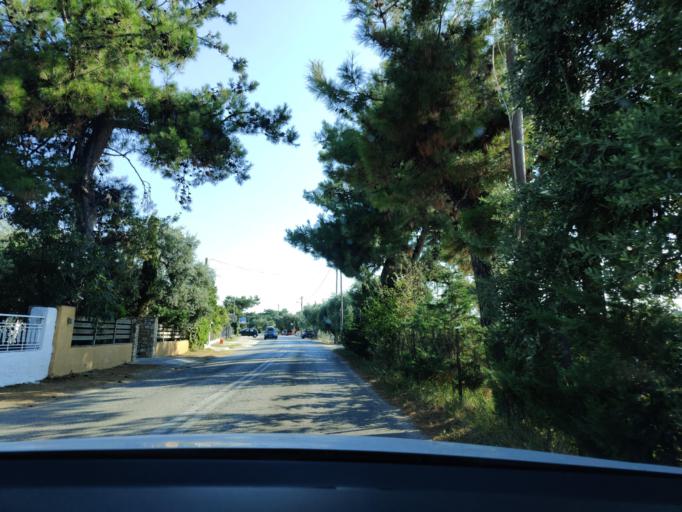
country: GR
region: East Macedonia and Thrace
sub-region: Nomos Kavalas
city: Prinos
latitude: 40.7004
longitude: 24.5282
